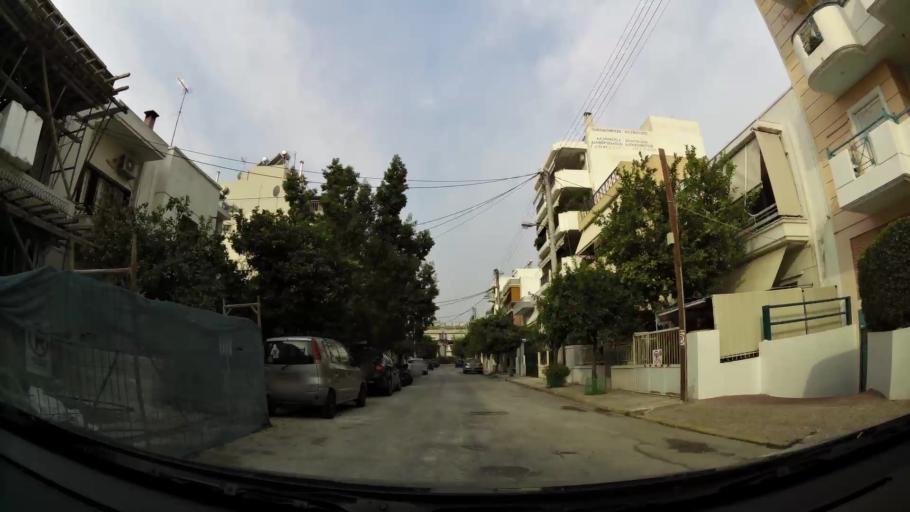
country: GR
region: Attica
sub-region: Nomarchia Athinas
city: Moskhaton
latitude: 37.9506
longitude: 23.6741
